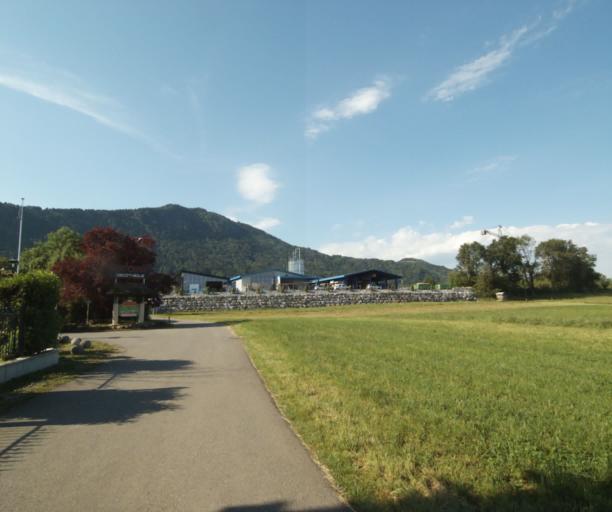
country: FR
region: Rhone-Alpes
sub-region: Departement de la Haute-Savoie
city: Allinges
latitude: 46.3176
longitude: 6.4881
